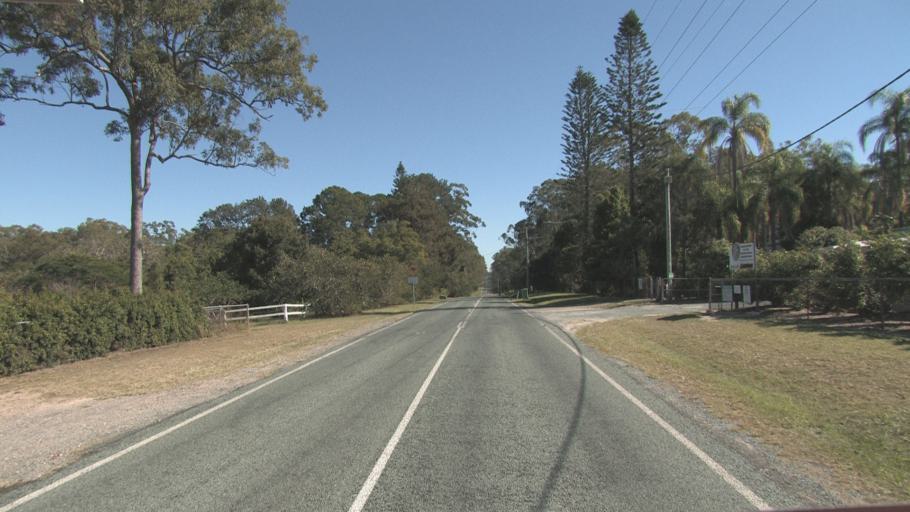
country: AU
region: Queensland
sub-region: Logan
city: Park Ridge South
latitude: -27.7185
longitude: 153.0552
